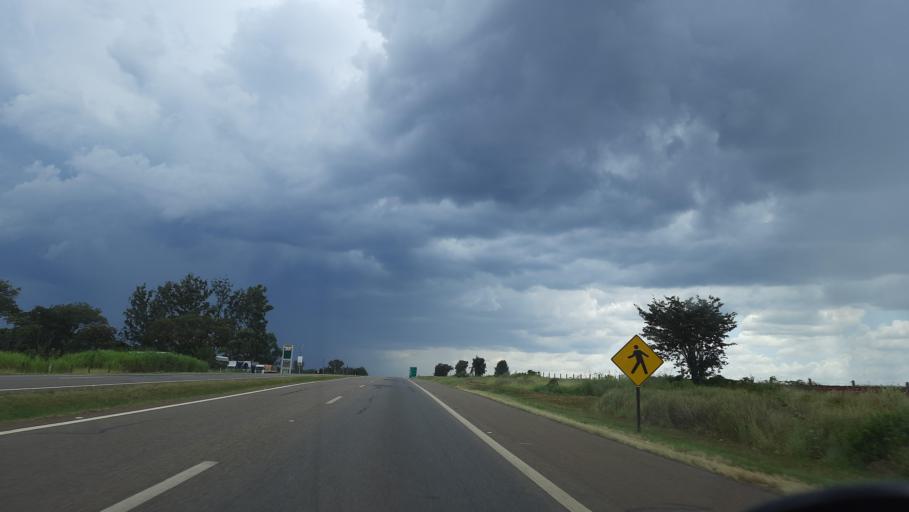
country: BR
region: Sao Paulo
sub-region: Aguai
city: Aguai
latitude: -22.0351
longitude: -47.0322
